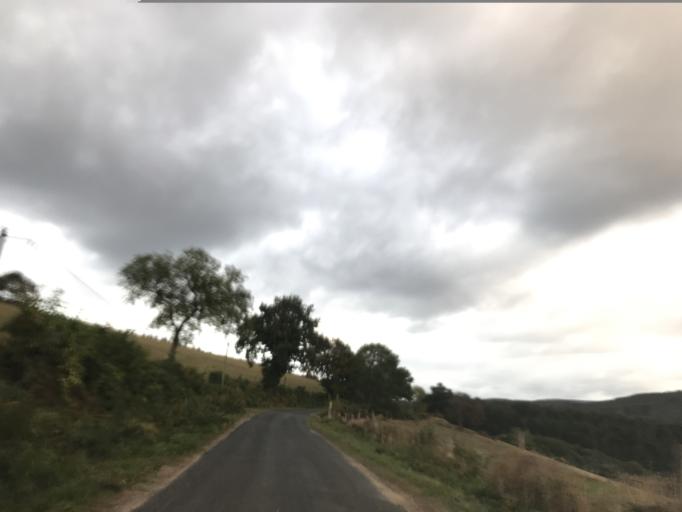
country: FR
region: Auvergne
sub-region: Departement du Puy-de-Dome
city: Celles-sur-Durolle
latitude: 45.8410
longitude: 3.6253
